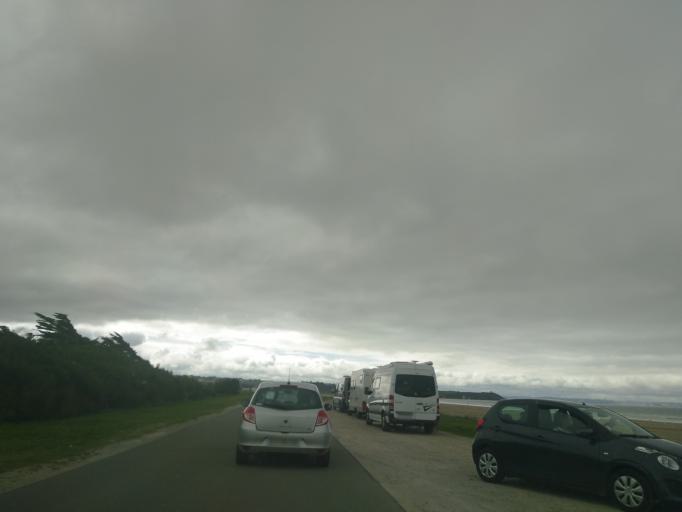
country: FR
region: Brittany
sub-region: Departement du Finistere
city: Plomodiern
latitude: 48.1890
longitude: -4.2993
